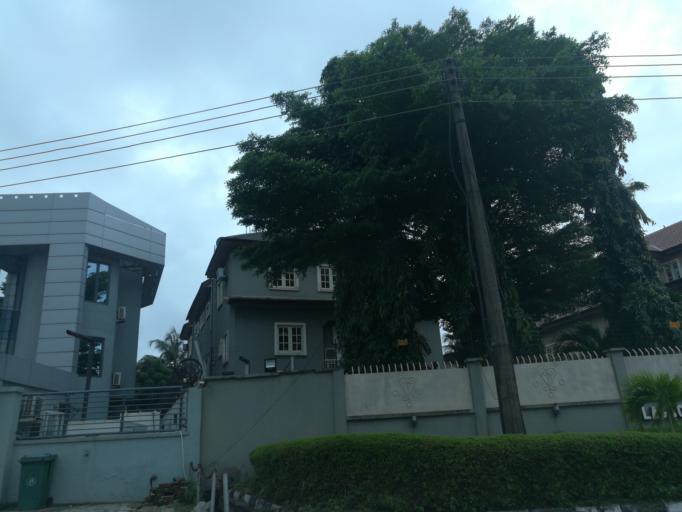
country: NG
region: Lagos
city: Ikoyi
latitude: 6.4449
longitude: 3.4543
